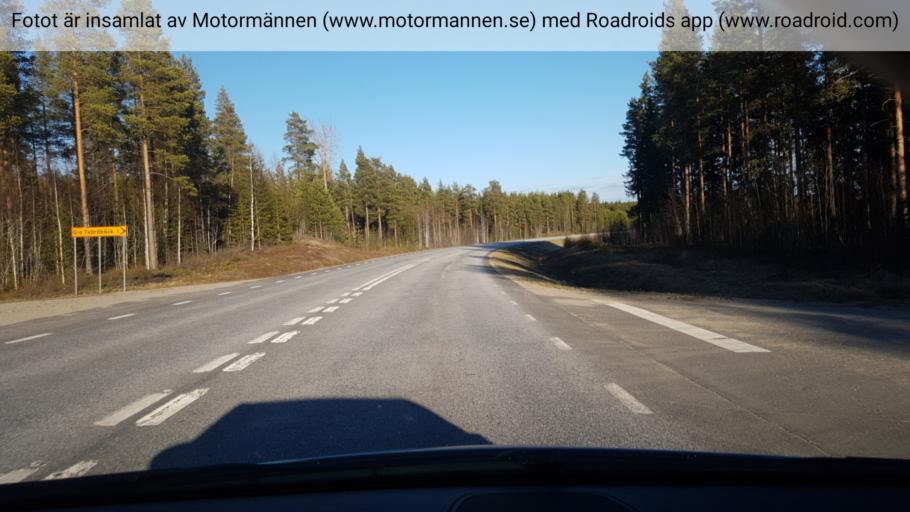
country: SE
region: Vaesterbotten
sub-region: Vannas Kommun
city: Vaennaes
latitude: 64.0074
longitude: 19.7131
